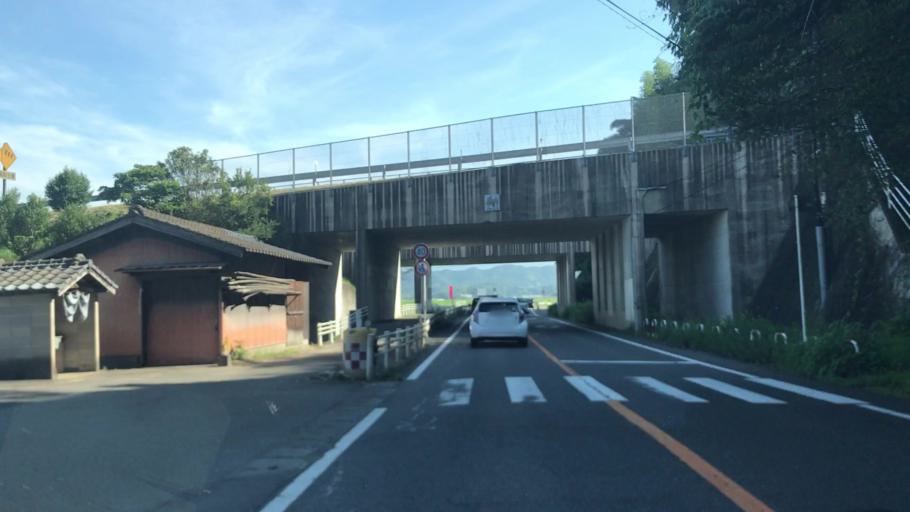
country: JP
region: Saga Prefecture
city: Takeocho-takeo
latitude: 33.2066
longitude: 130.0577
